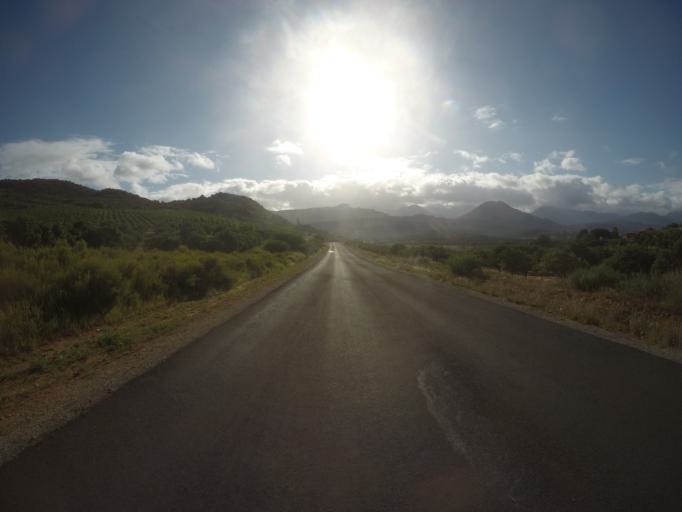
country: ZA
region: Western Cape
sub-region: West Coast District Municipality
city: Clanwilliam
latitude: -32.4311
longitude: 18.9508
